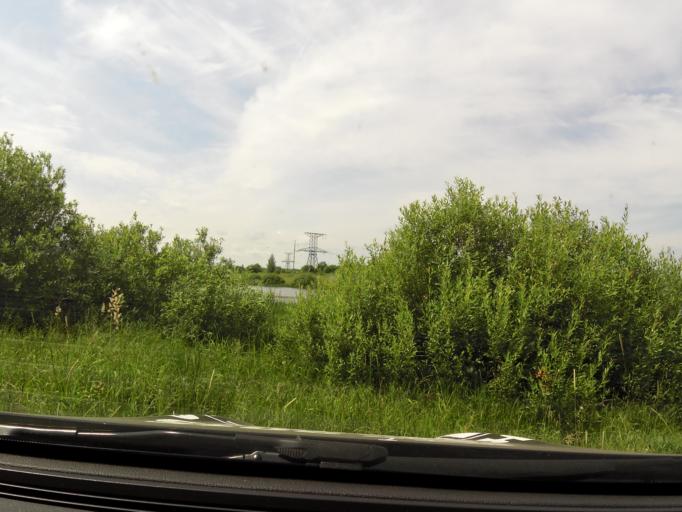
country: RU
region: Kostroma
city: Galich
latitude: 58.3746
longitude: 42.3968
